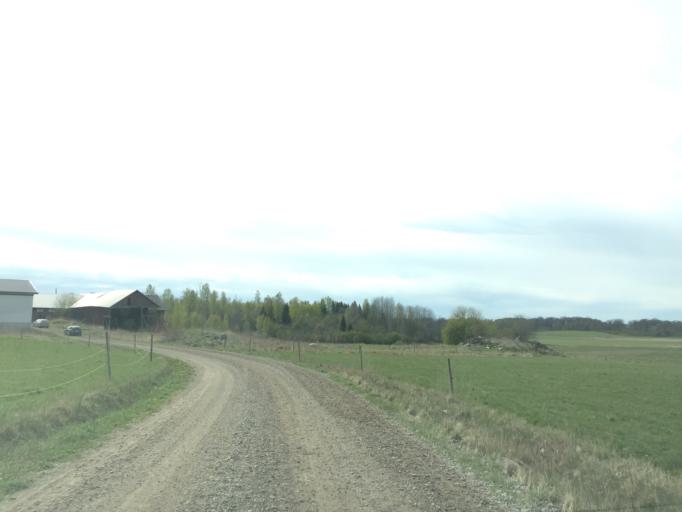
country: SE
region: OErebro
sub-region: Lekebergs Kommun
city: Fjugesta
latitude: 59.0609
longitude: 14.9164
